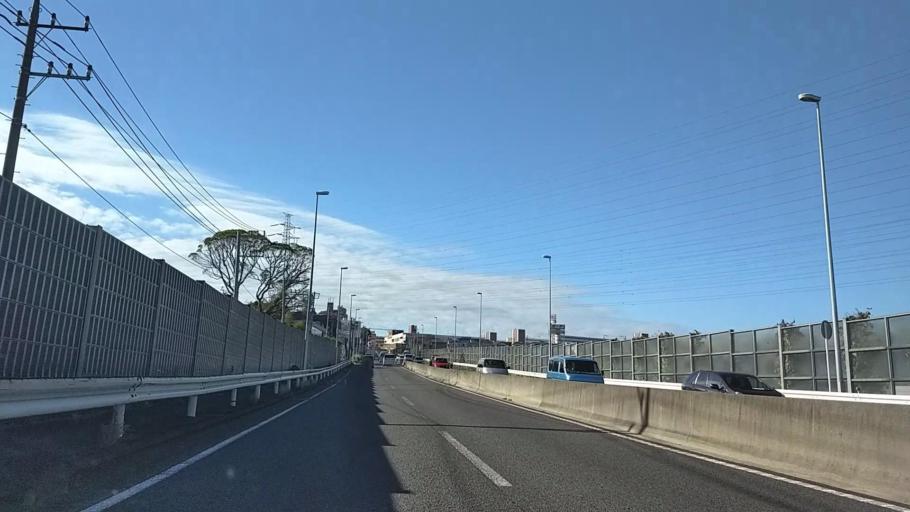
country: JP
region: Kanagawa
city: Fujisawa
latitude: 35.3933
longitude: 139.5247
